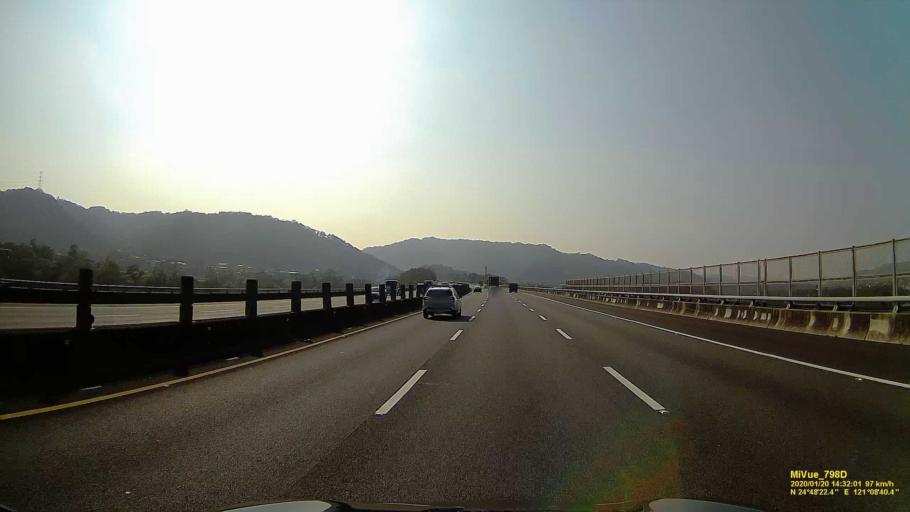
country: TW
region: Taiwan
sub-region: Hsinchu
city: Zhubei
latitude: 24.8058
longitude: 121.1442
